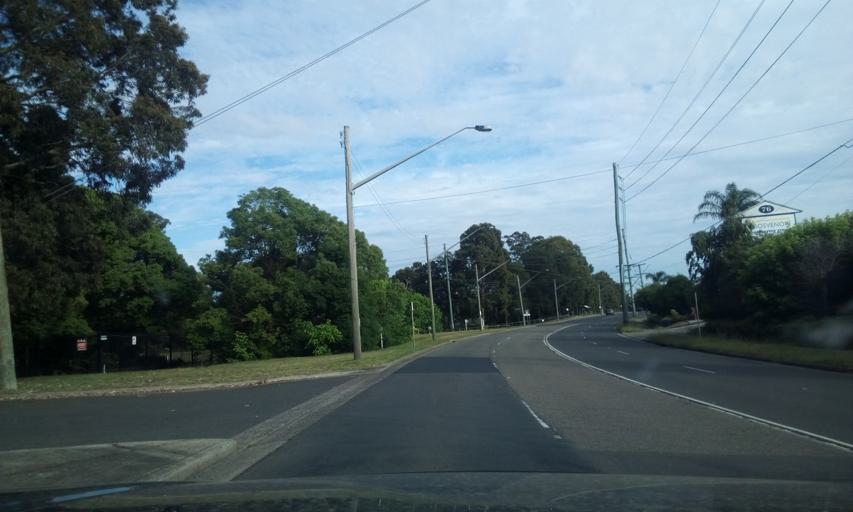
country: AU
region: New South Wales
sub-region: Fairfield
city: Liverpool
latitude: -33.9361
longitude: 150.9353
